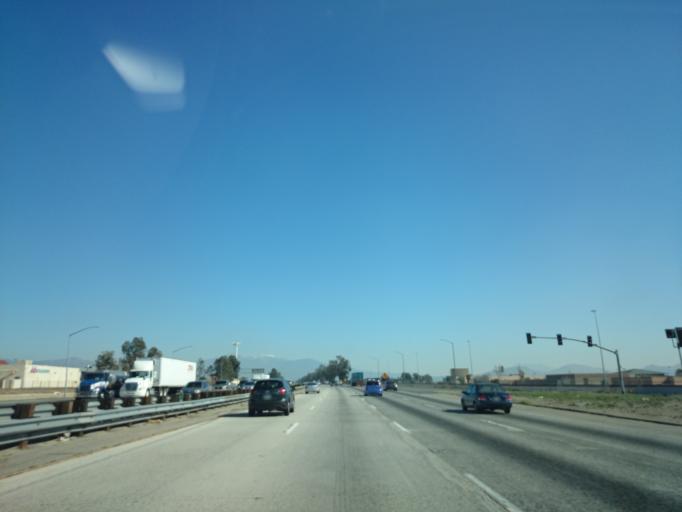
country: US
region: California
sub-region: San Bernardino County
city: Fontana
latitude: 34.0673
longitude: -117.4339
